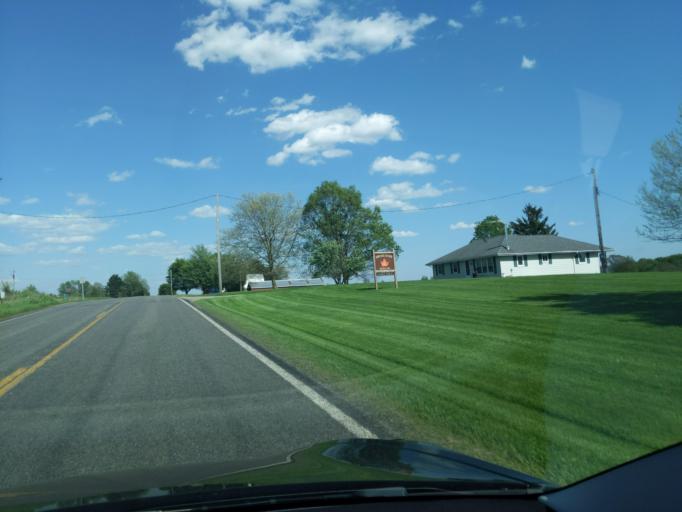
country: US
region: Michigan
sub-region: Ionia County
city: Lake Odessa
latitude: 42.7842
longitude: -85.2067
